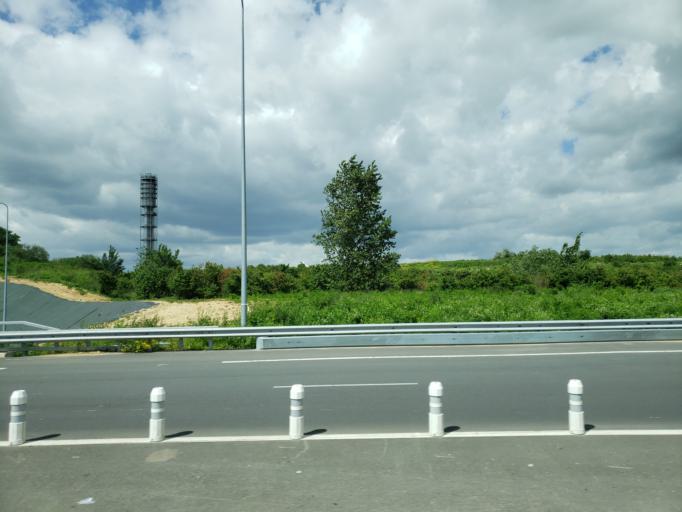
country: FR
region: Ile-de-France
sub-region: Departement de Seine-et-Marne
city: Mitry-Mory
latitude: 49.0072
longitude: 2.6015
